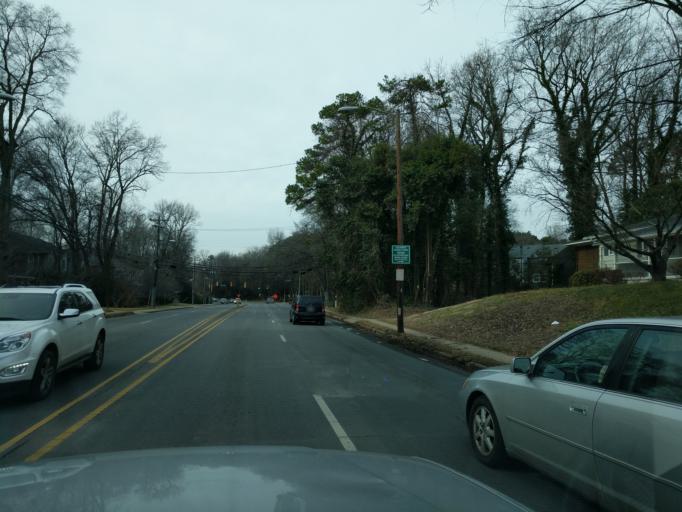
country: US
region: North Carolina
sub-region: Mecklenburg County
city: Charlotte
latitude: 35.1725
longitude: -80.8570
